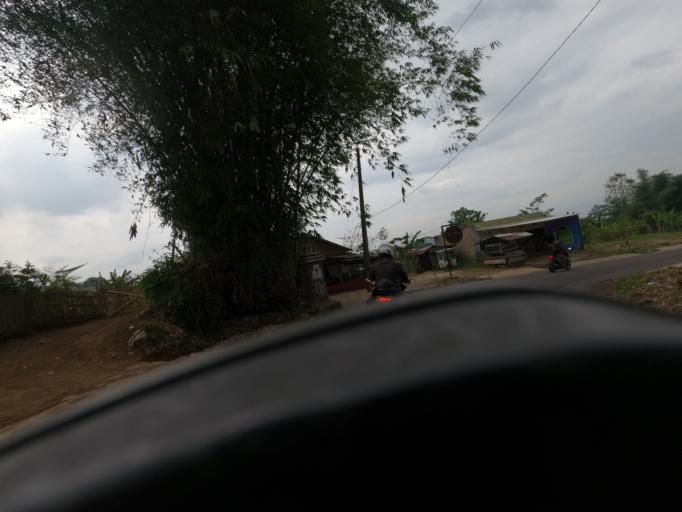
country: ID
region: West Java
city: Padalarang
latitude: -6.8373
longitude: 107.5130
